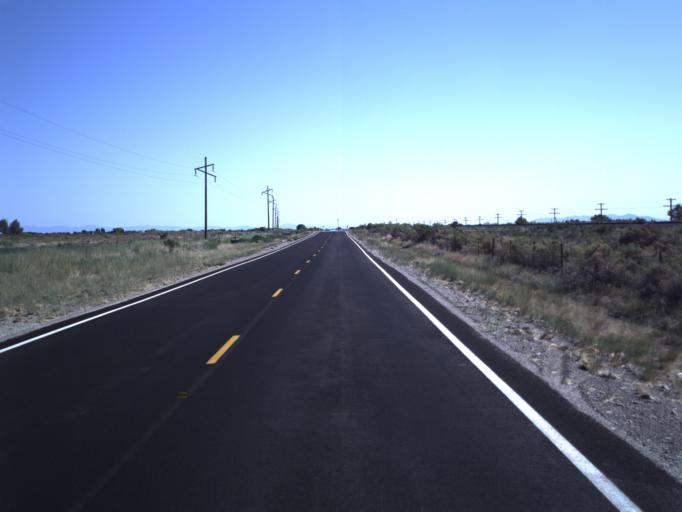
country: US
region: Utah
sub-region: Millard County
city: Delta
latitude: 39.2482
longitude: -112.6580
